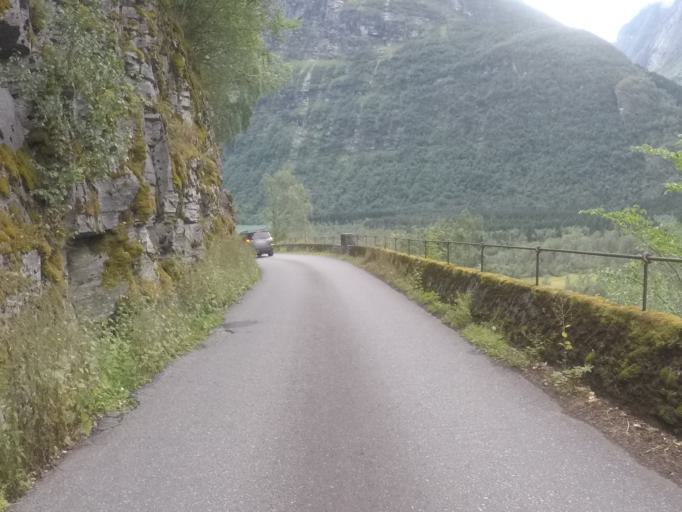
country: NO
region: Sogn og Fjordane
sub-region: Stryn
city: Stryn
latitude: 61.7899
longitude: 6.9979
